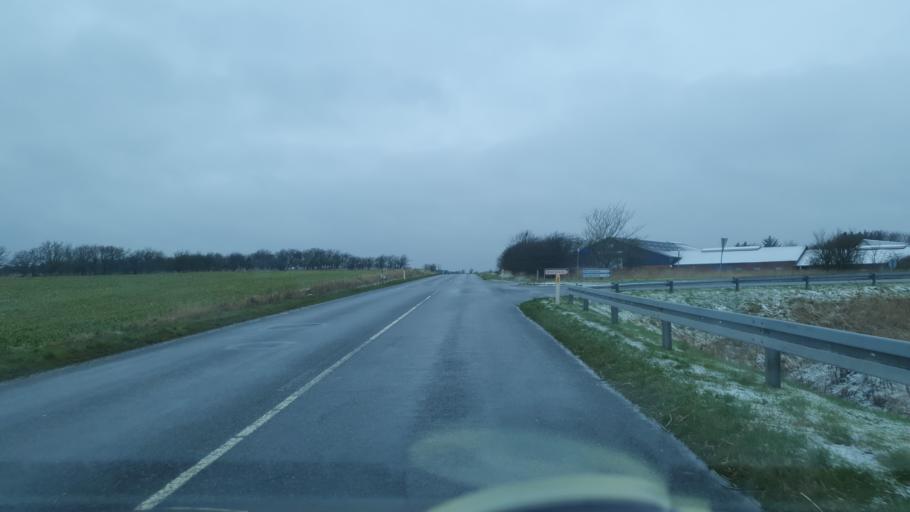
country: DK
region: North Denmark
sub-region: Jammerbugt Kommune
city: Brovst
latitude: 57.1224
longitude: 9.4921
